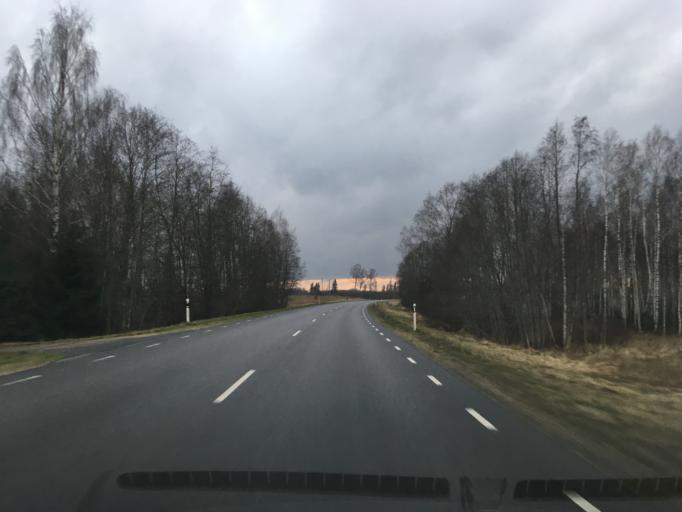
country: EE
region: Harju
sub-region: Anija vald
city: Kehra
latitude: 59.2237
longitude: 25.2671
